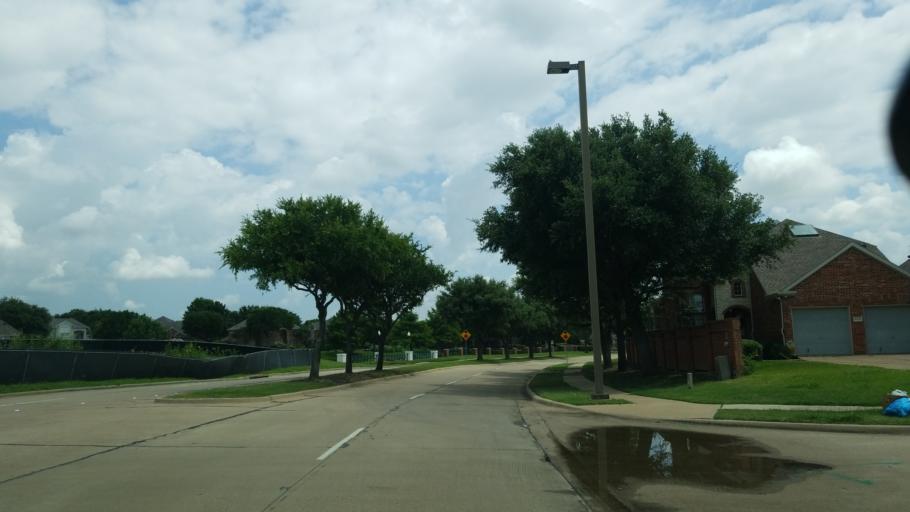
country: US
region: Texas
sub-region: Dallas County
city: Coppell
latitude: 32.9373
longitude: -96.9626
